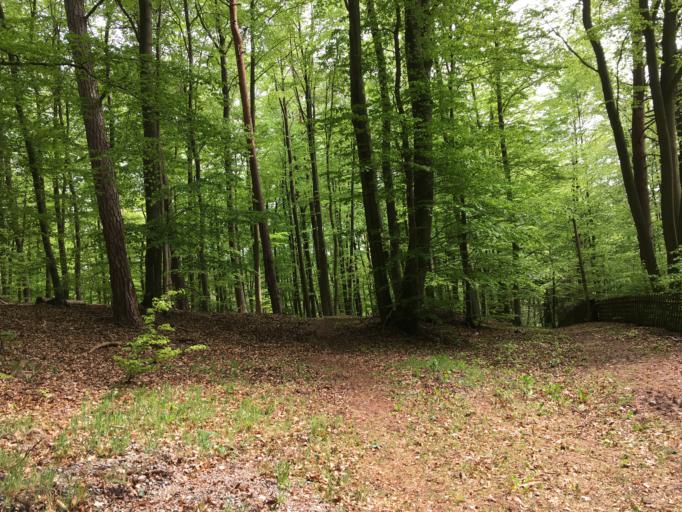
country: DE
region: Brandenburg
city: Wandlitz
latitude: 52.7594
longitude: 13.5324
